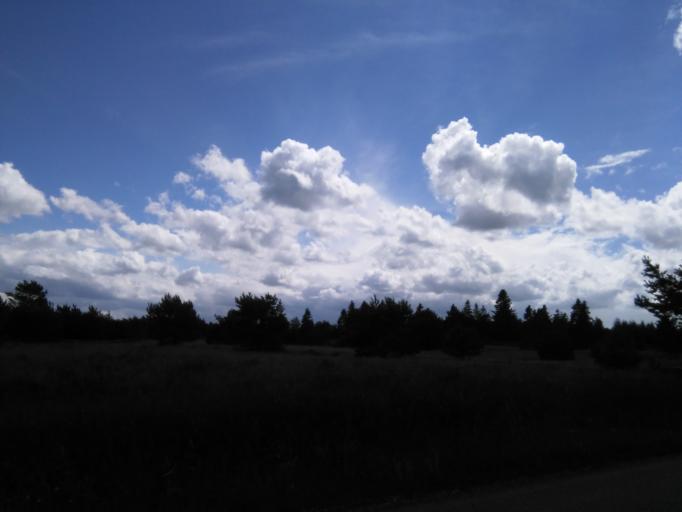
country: DK
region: Central Jutland
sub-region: Silkeborg Kommune
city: Virklund
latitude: 56.0888
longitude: 9.4308
